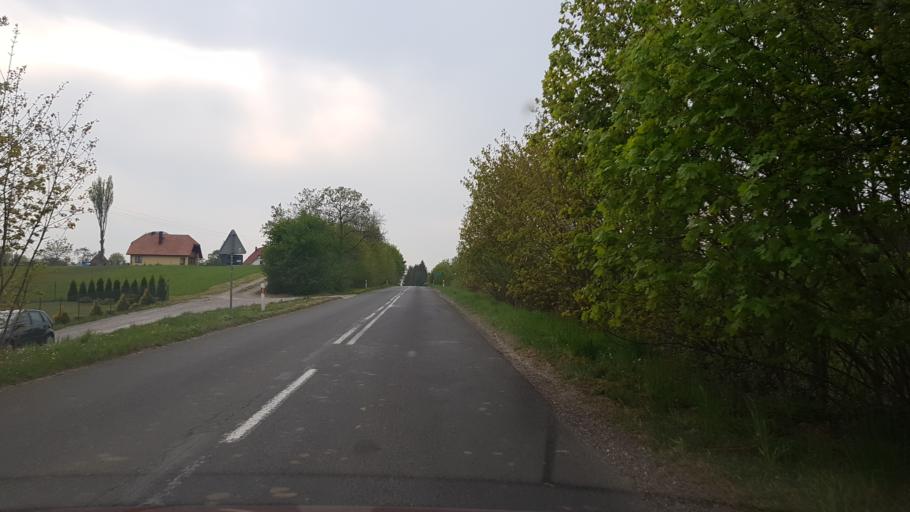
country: PL
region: West Pomeranian Voivodeship
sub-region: Powiat gryfinski
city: Stare Czarnowo
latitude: 53.2887
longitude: 14.7290
